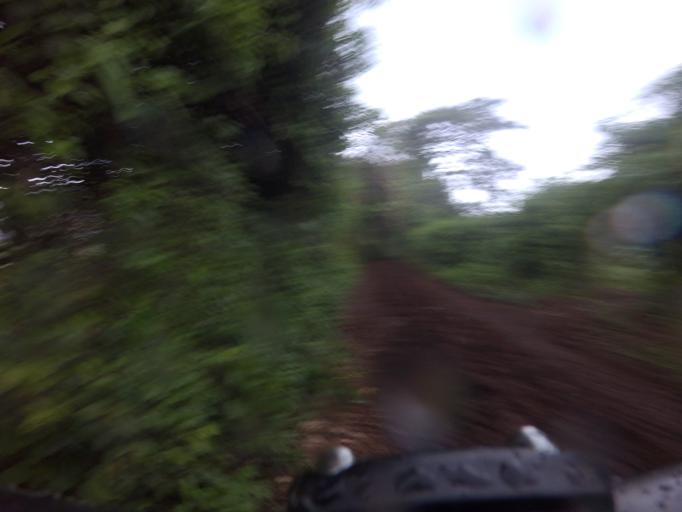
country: CU
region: Pinar del Rio
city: Vinales
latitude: 22.6171
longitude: -83.7158
